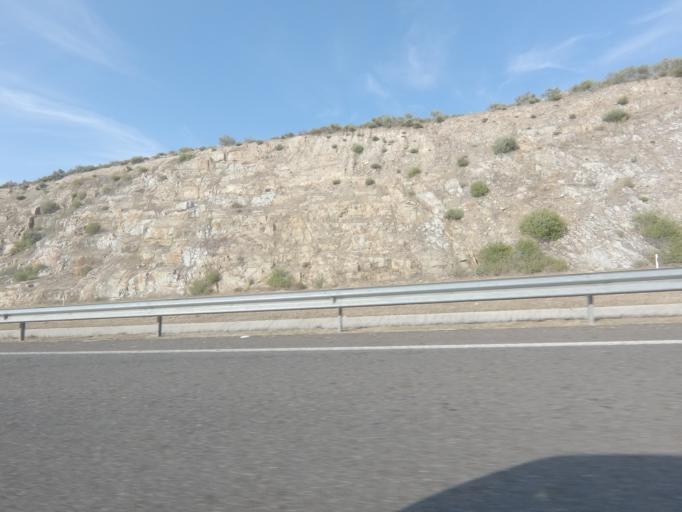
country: ES
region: Galicia
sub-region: Provincia de Ourense
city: Oimbra
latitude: 41.8602
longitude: -7.4258
